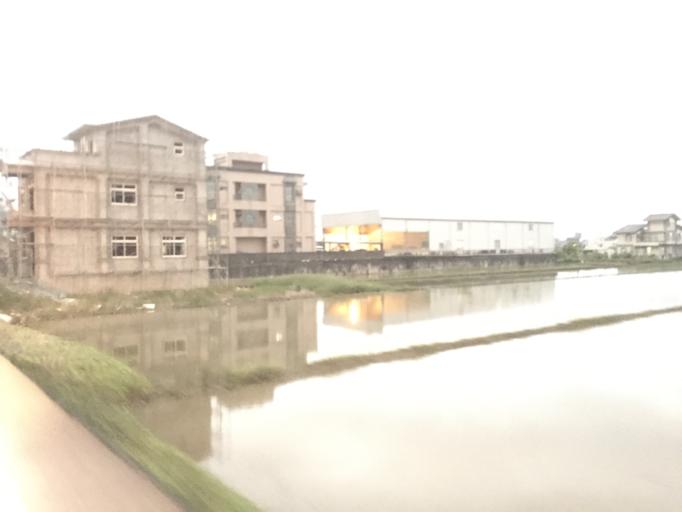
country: TW
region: Taiwan
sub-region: Yilan
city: Yilan
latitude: 24.7702
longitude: 121.7432
